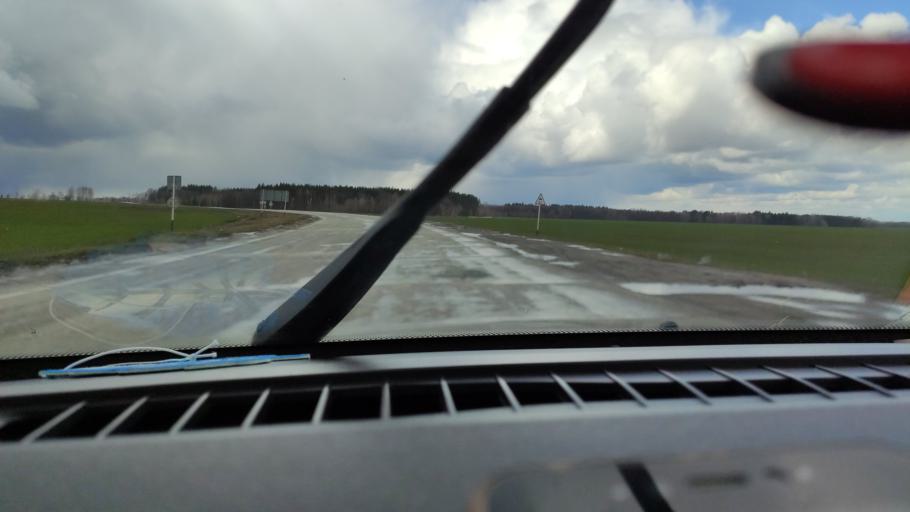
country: RU
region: Samara
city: Povolzhskiy
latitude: 53.8054
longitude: 49.7910
